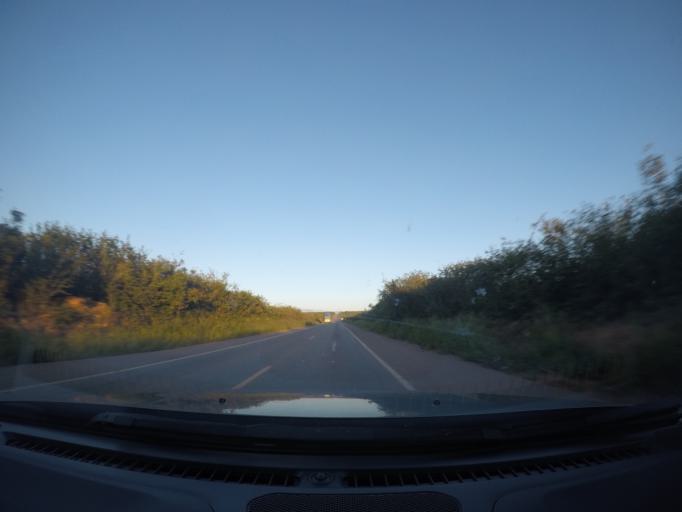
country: BR
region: Bahia
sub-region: Seabra
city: Seabra
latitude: -12.3930
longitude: -41.9218
